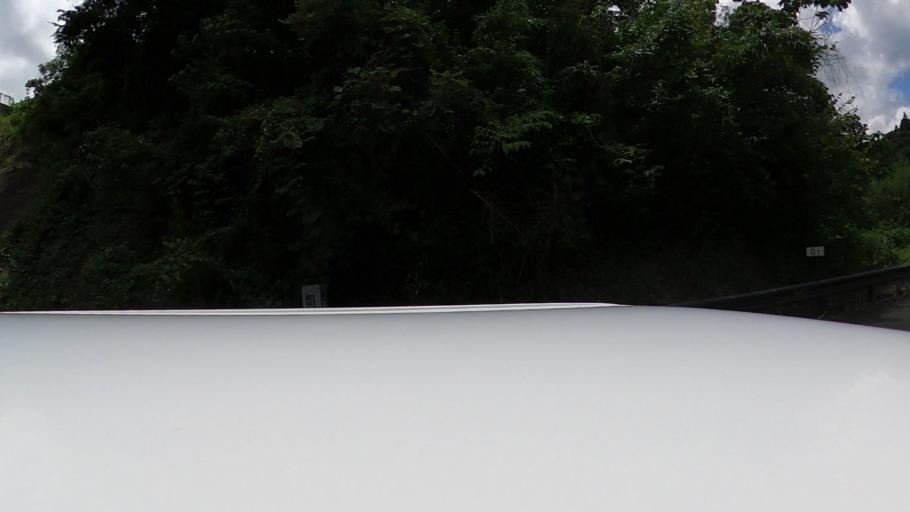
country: JP
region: Miyazaki
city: Nobeoka
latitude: 32.5942
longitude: 131.4983
